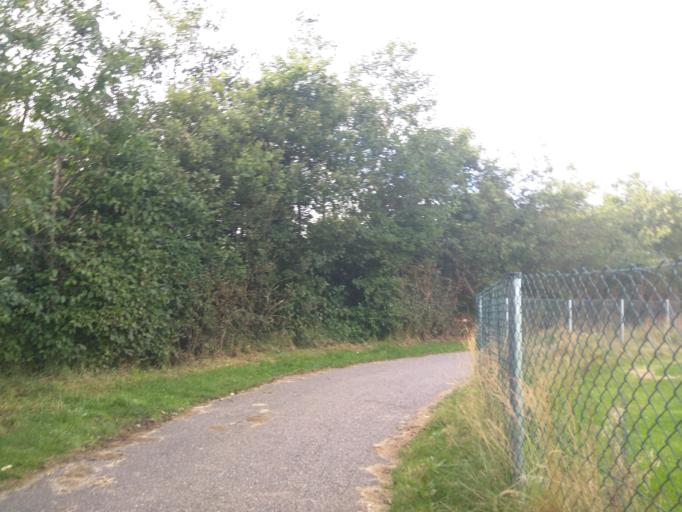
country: DK
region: Central Jutland
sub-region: Viborg Kommune
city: Viborg
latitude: 56.4415
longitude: 9.3764
